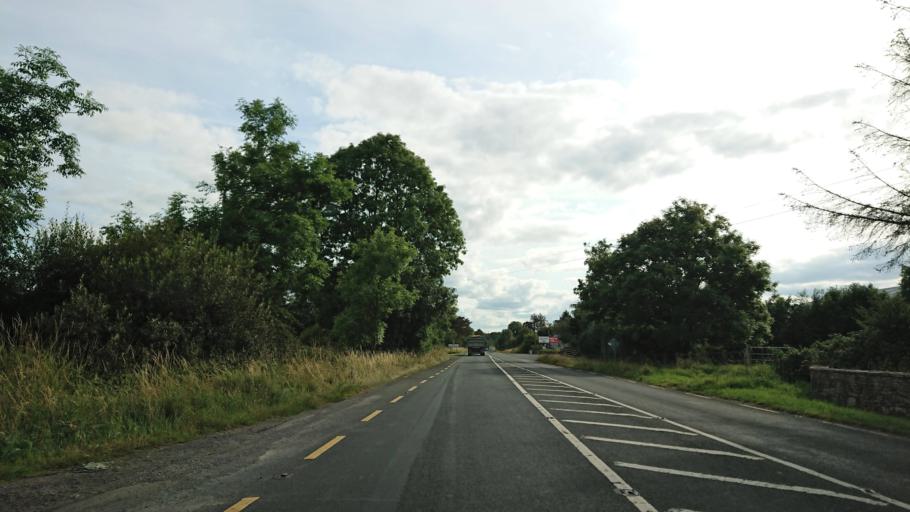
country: IE
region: Connaught
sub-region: County Leitrim
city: Carrick-on-Shannon
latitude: 53.9729
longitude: -8.0626
